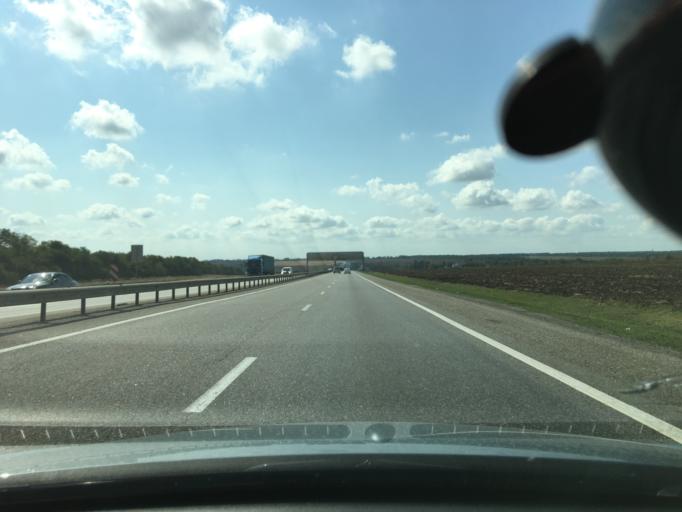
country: RU
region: Krasnodarskiy
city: Krasnoye
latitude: 46.7799
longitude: 39.6646
